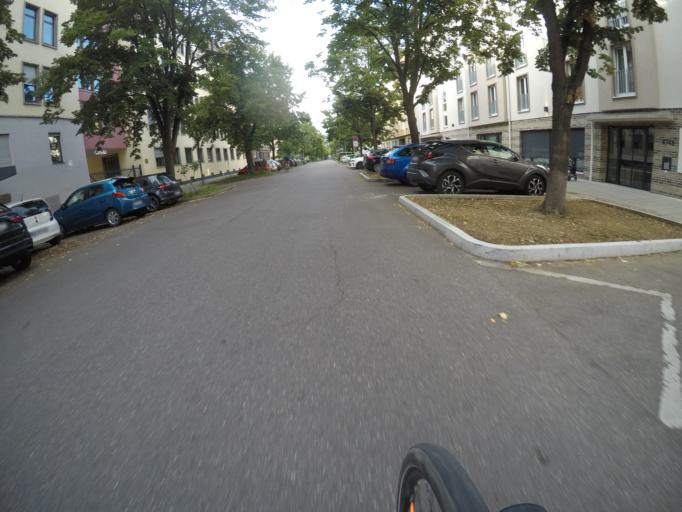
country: DE
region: Baden-Wuerttemberg
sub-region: Regierungsbezirk Stuttgart
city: Stuttgart
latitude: 48.7740
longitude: 9.1642
